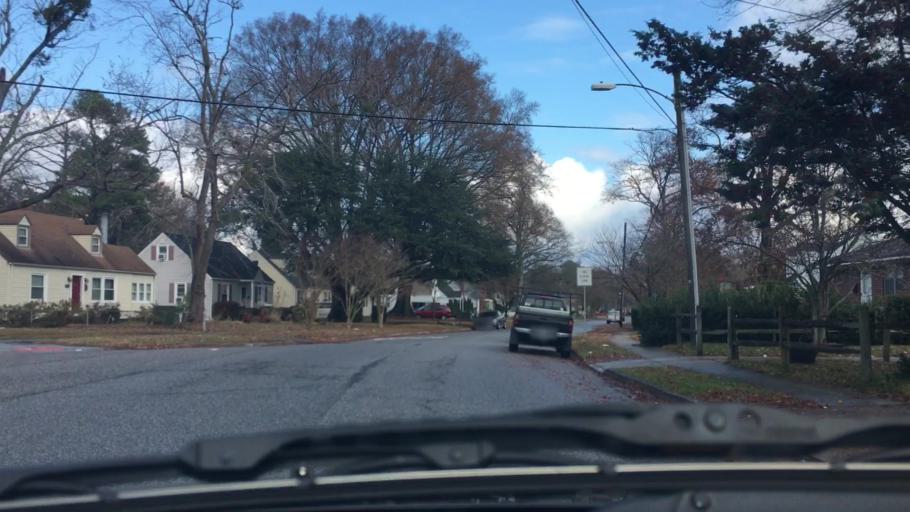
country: US
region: Virginia
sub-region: City of Norfolk
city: Norfolk
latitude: 36.9192
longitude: -76.2497
